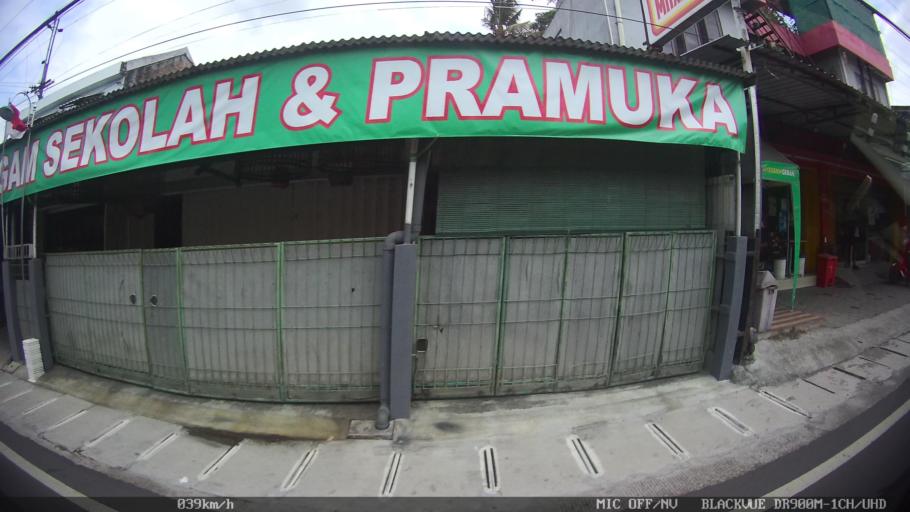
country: ID
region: Central Java
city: Candi Prambanan
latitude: -7.8046
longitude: 110.4828
